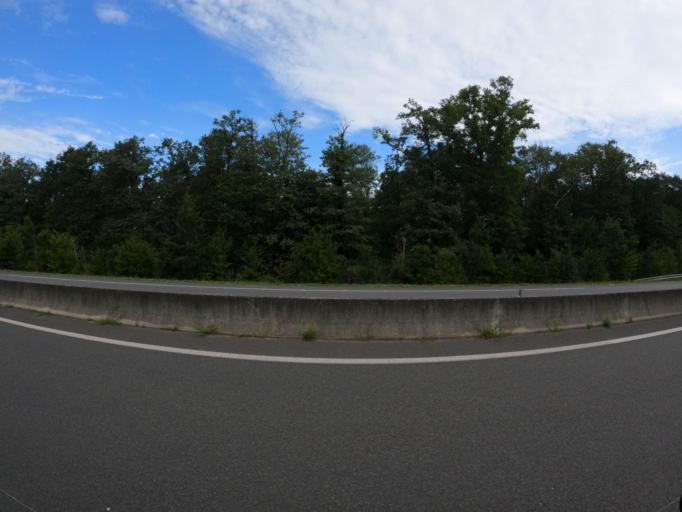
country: FR
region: Centre
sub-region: Departement d'Indre-et-Loire
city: Langeais
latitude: 47.3184
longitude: 0.3258
